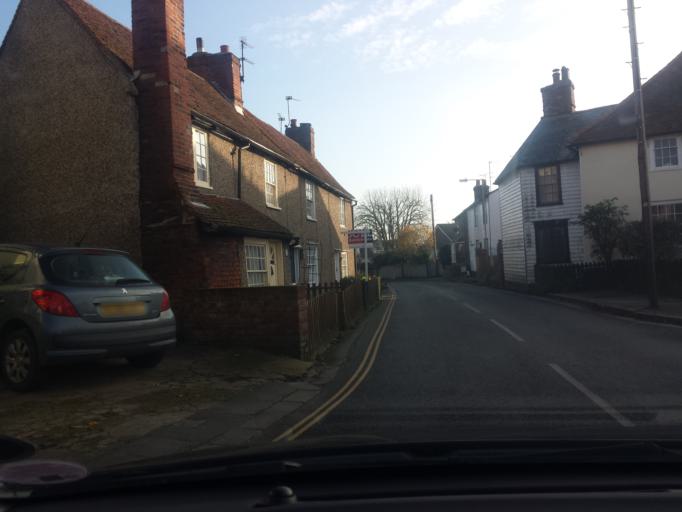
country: GB
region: England
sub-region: Essex
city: Saint Osyth
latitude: 51.7983
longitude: 1.0780
